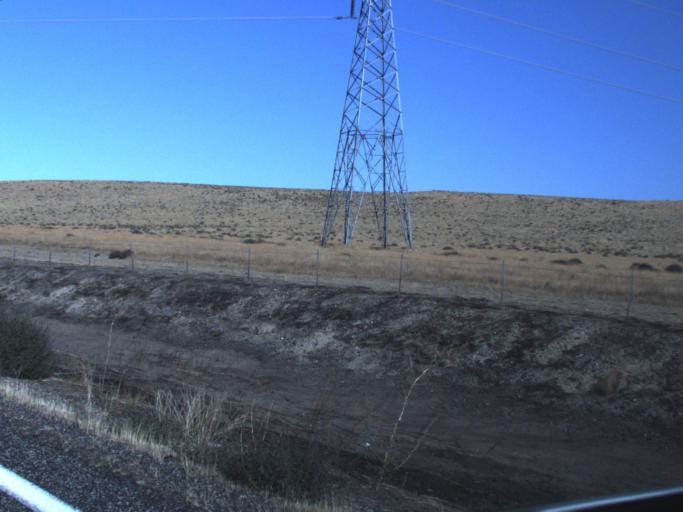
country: US
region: Washington
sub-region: Grant County
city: Desert Aire
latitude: 46.5603
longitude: -119.7082
